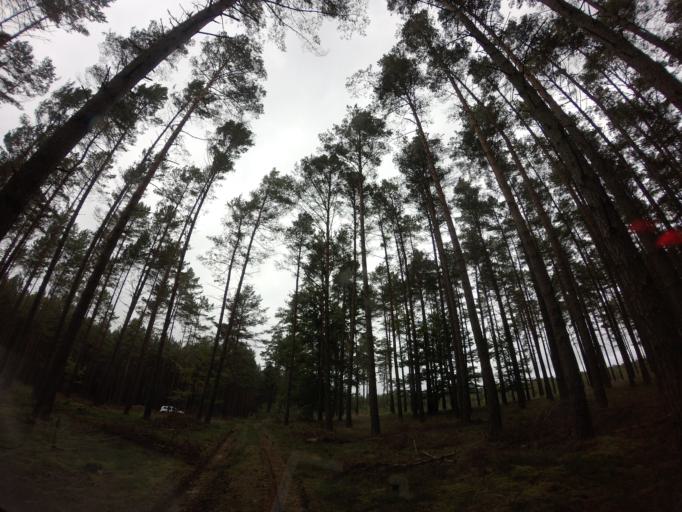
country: PL
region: West Pomeranian Voivodeship
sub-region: Powiat choszczenski
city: Drawno
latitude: 53.1398
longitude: 15.7676
